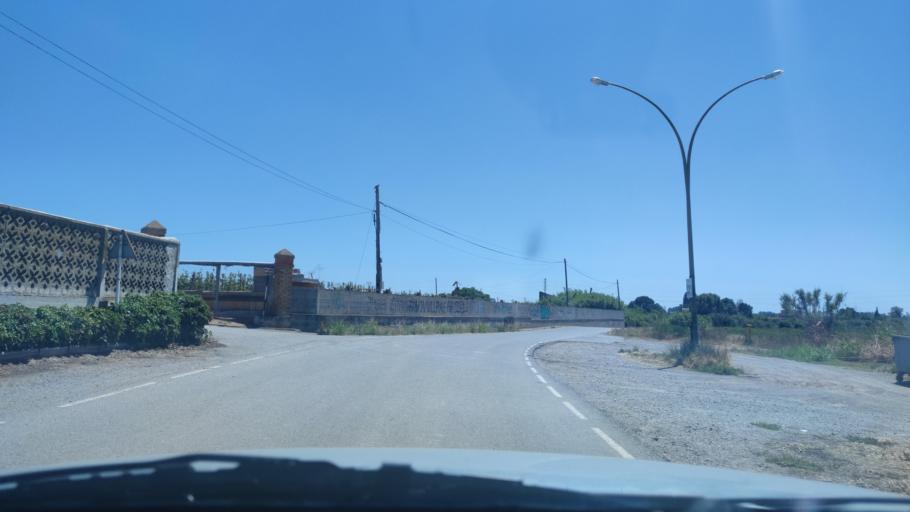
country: ES
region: Catalonia
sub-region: Provincia de Lleida
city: Alcoletge
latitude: 41.6417
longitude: 0.6620
